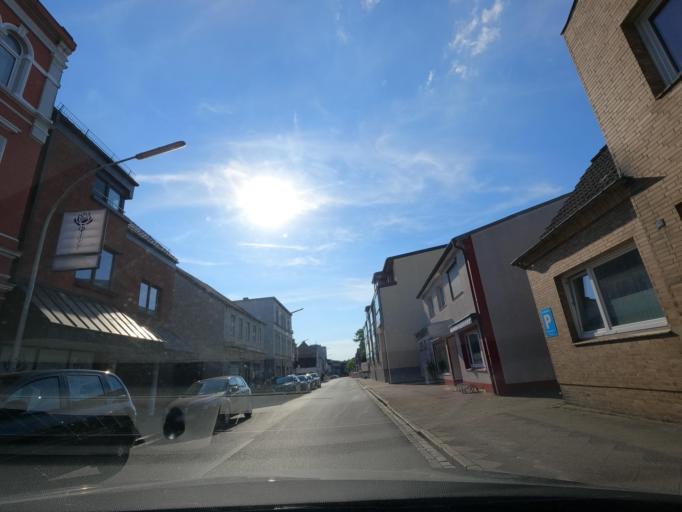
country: DE
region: Schleswig-Holstein
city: Uetersen
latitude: 53.6820
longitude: 9.6699
